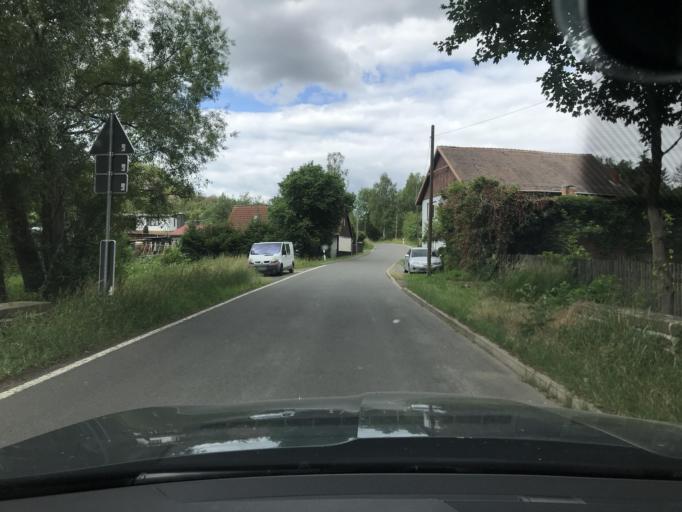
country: DE
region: Saxony-Anhalt
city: Friedrichsbrunn
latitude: 51.6186
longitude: 11.0582
